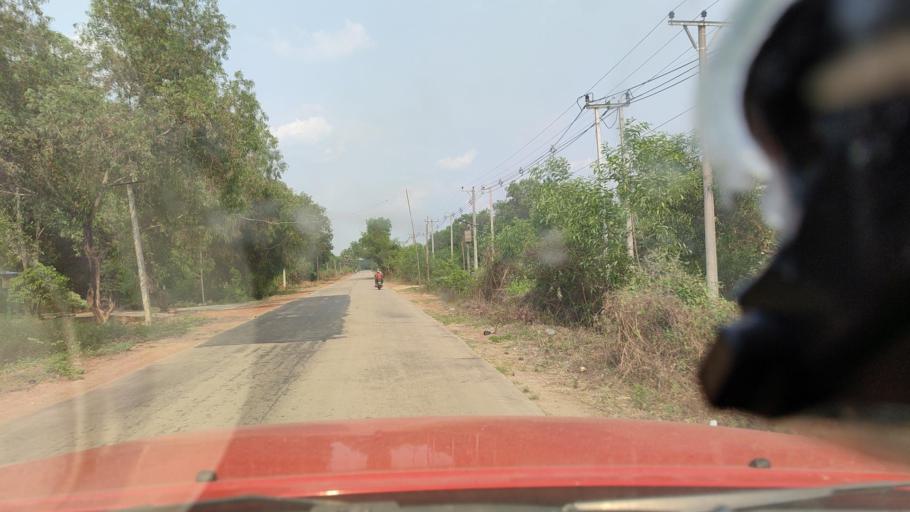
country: MM
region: Ayeyarwady
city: Nyaungdon
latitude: 17.1604
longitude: 95.9186
